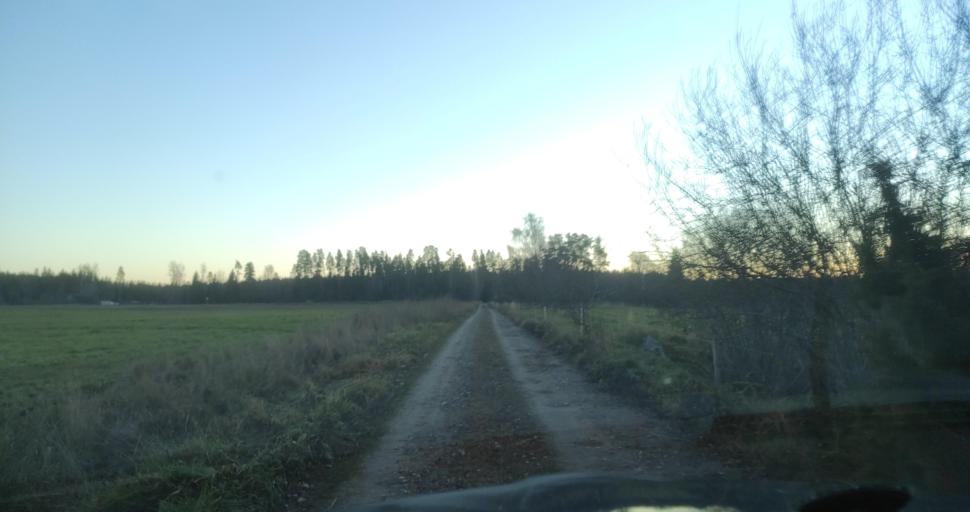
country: LV
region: Dundaga
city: Dundaga
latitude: 57.3730
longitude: 22.2257
